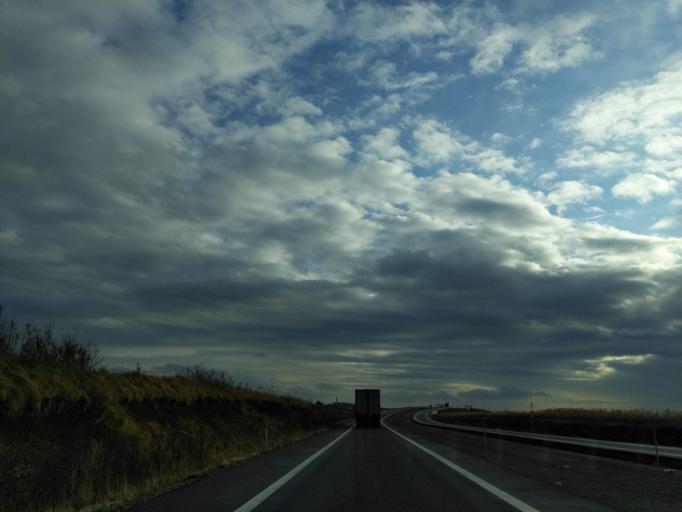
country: JP
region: Hokkaido
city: Chitose
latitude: 42.9403
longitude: 141.7145
